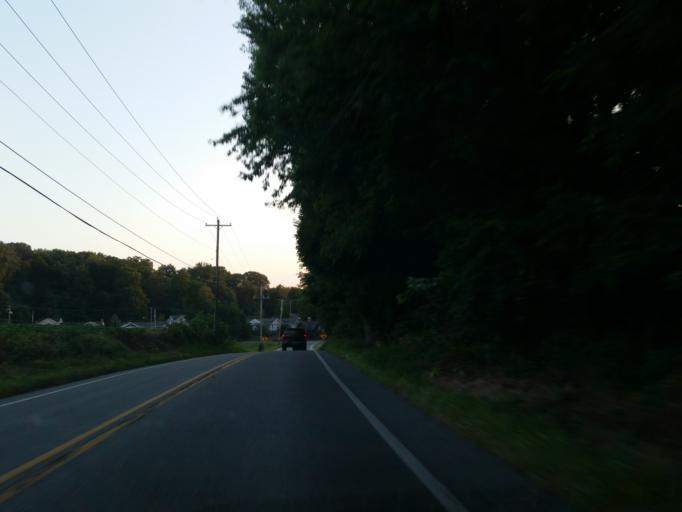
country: US
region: Pennsylvania
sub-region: Lebanon County
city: Cornwall
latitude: 40.2780
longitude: -76.4098
